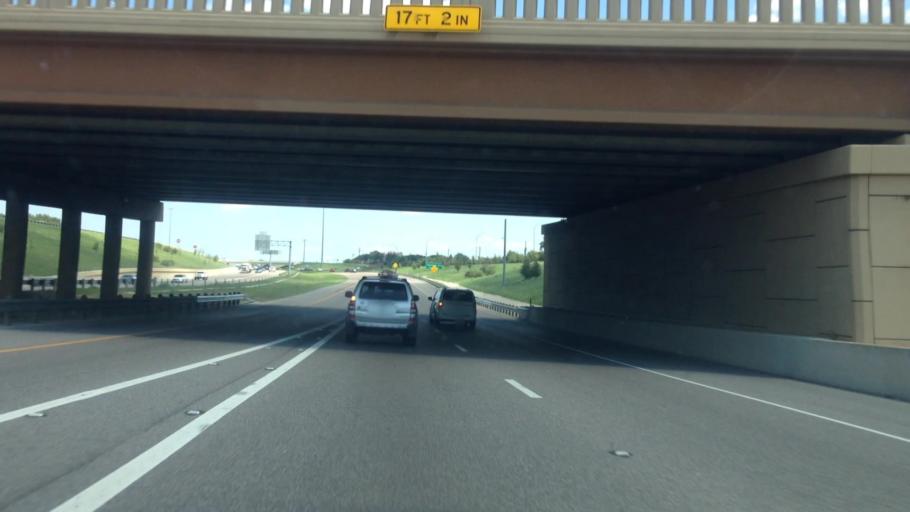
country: US
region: Texas
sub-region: Tarrant County
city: Bedford
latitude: 32.8392
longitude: -97.1205
